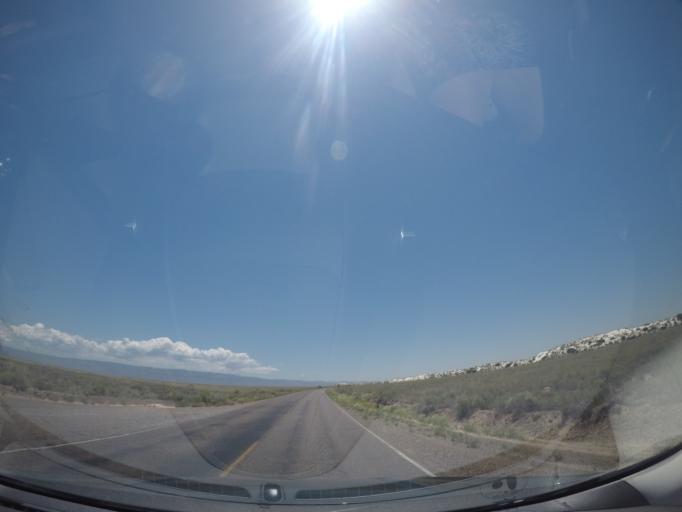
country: US
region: New Mexico
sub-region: Otero County
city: Holloman Air Force Base
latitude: 32.7921
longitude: -106.1986
